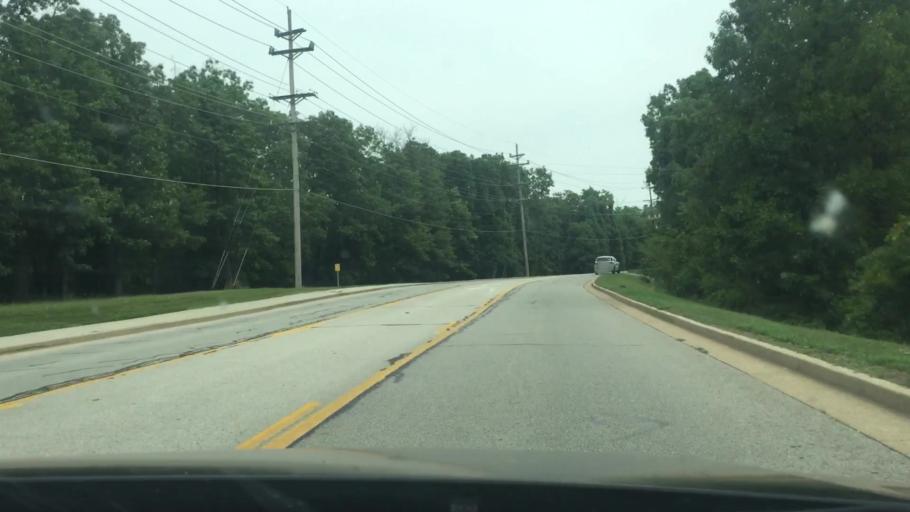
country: US
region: Missouri
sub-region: Camden County
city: Four Seasons
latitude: 38.1938
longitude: -92.6783
